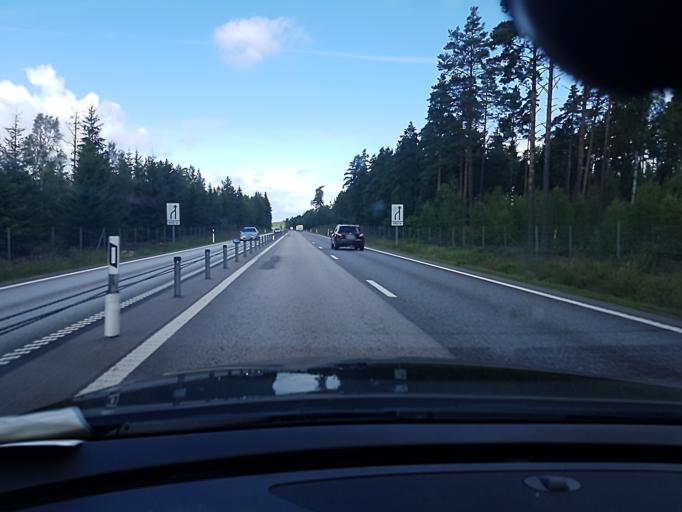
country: SE
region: Kronoberg
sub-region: Lessebo Kommun
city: Hovmantorp
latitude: 56.8247
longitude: 15.0873
